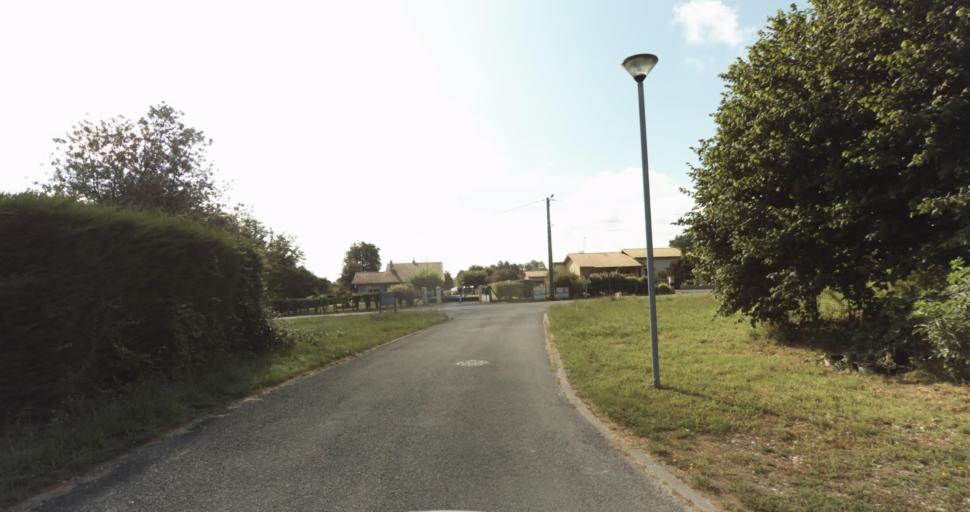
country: FR
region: Aquitaine
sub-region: Departement de la Gironde
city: Bazas
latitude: 44.4354
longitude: -0.2416
